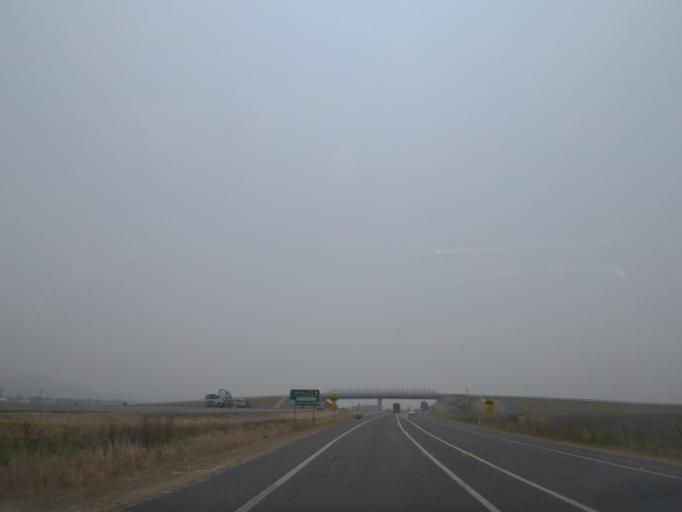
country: AU
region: New South Wales
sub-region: Clarence Valley
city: Maclean
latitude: -29.3950
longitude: 153.2393
